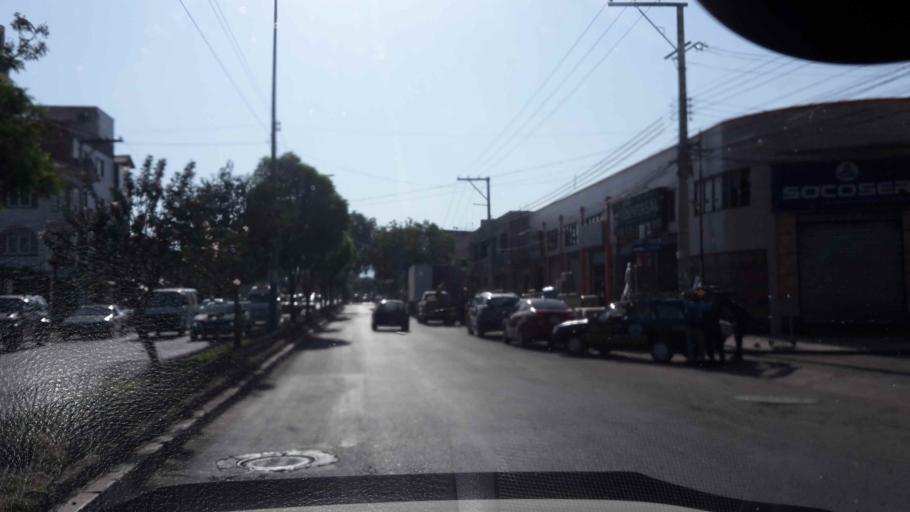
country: BO
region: Cochabamba
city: Cochabamba
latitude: -17.4018
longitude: -66.1646
